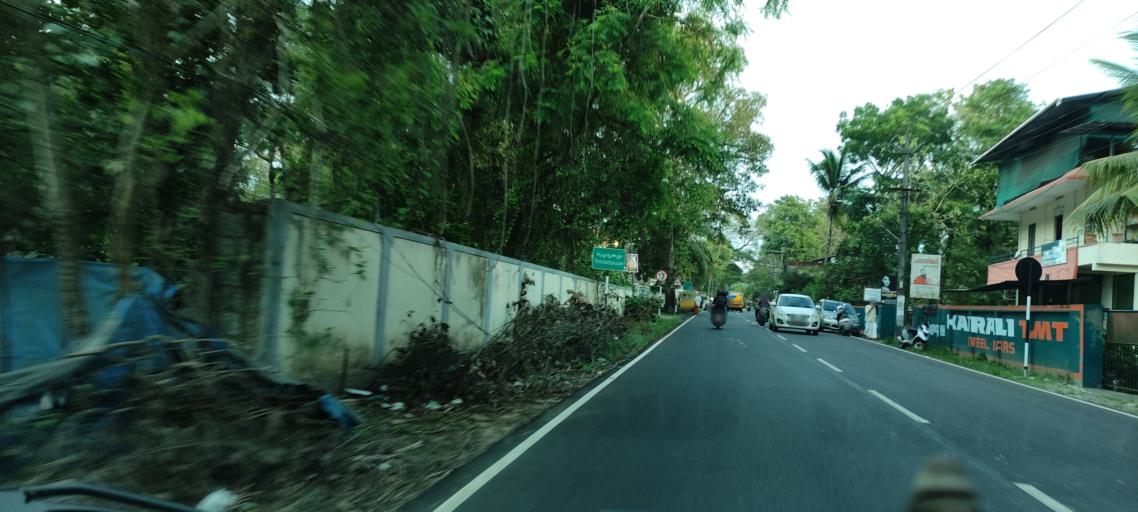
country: IN
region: Kerala
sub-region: Alappuzha
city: Kutiatodu
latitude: 9.8350
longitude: 76.3334
